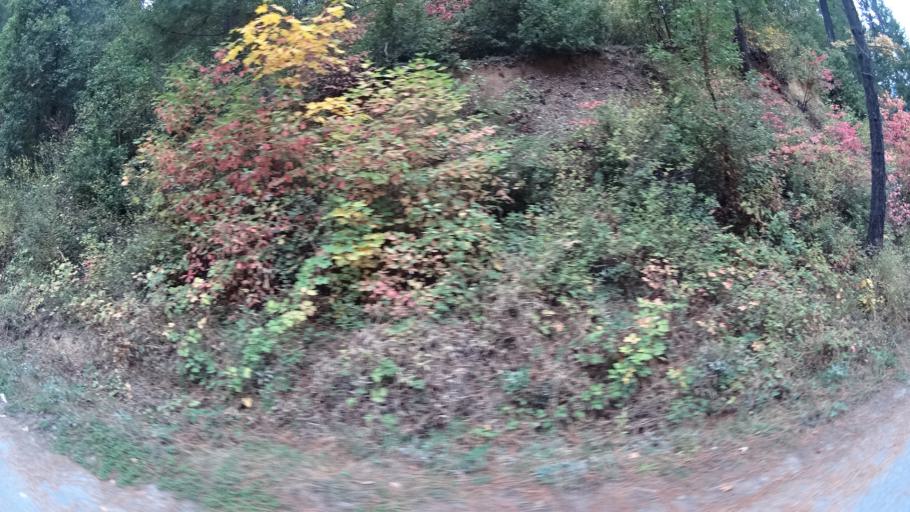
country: US
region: California
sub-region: Siskiyou County
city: Happy Camp
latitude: 41.8232
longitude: -123.3845
